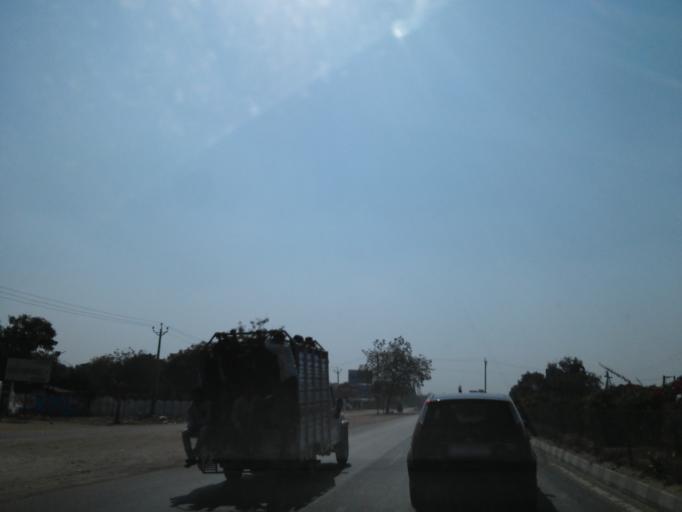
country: IN
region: Gujarat
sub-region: Gandhinagar
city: Adalaj
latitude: 23.1568
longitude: 72.5541
